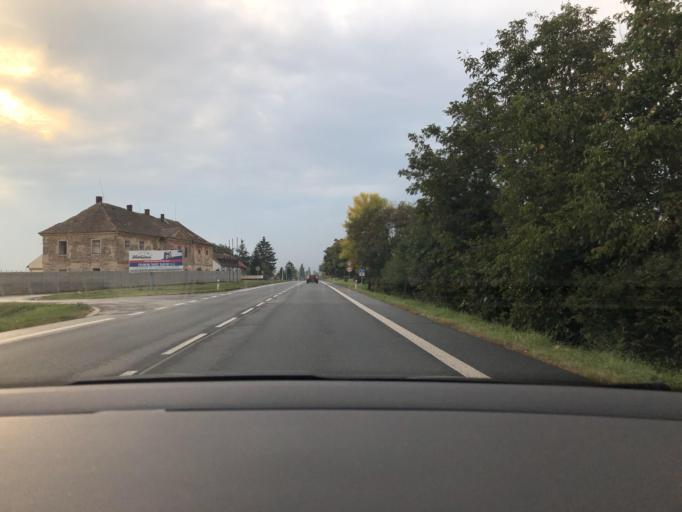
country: CZ
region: Central Bohemia
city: Velim
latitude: 50.0393
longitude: 15.1123
